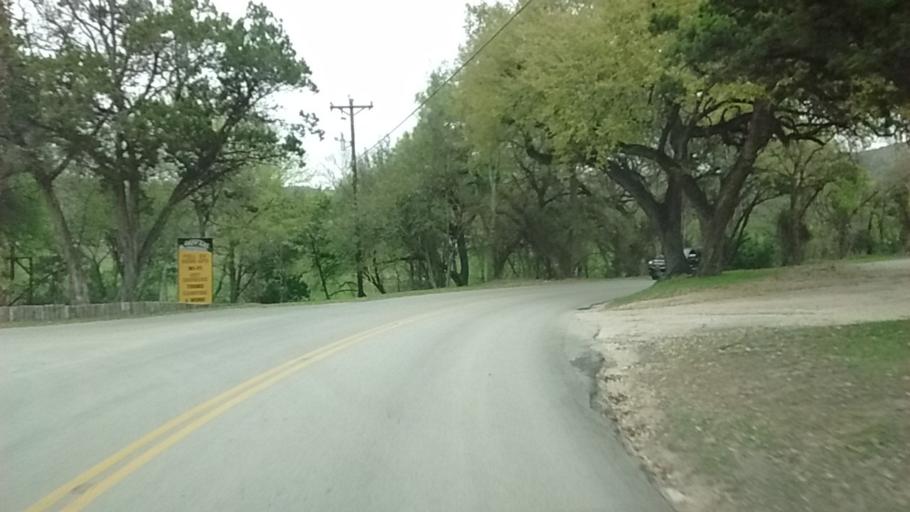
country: US
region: Texas
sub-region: Comal County
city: Canyon Lake
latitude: 29.8182
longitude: -98.1728
